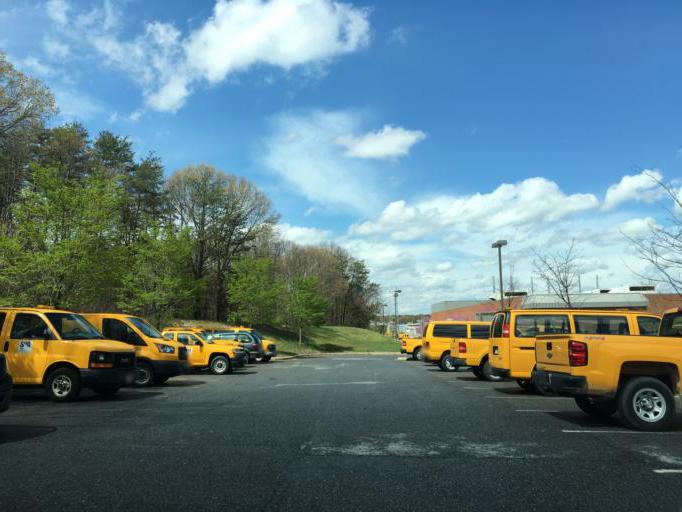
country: US
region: Maryland
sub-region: Anne Arundel County
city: Severn
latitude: 39.1561
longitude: -76.6782
